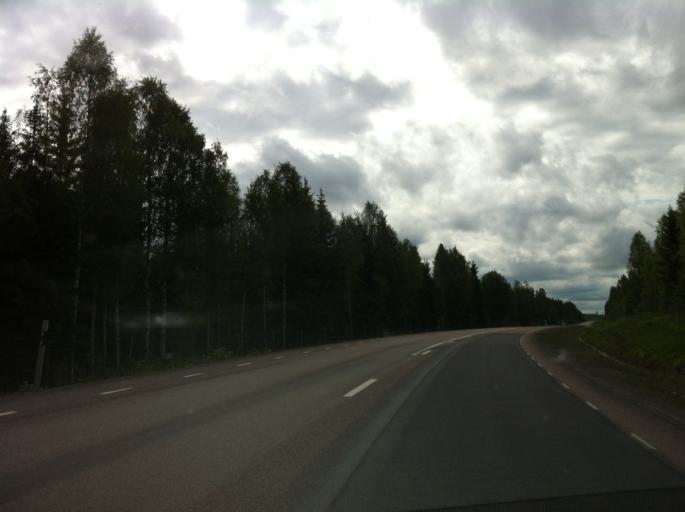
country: SE
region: Vaermland
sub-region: Sunne Kommun
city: Sunne
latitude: 59.7645
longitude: 13.1100
